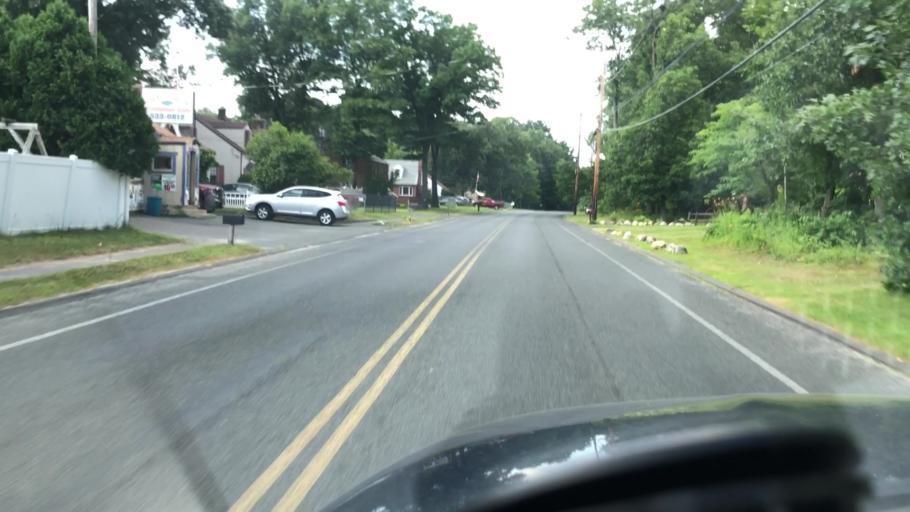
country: US
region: Massachusetts
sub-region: Hampshire County
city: Southampton
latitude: 42.1852
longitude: -72.6868
